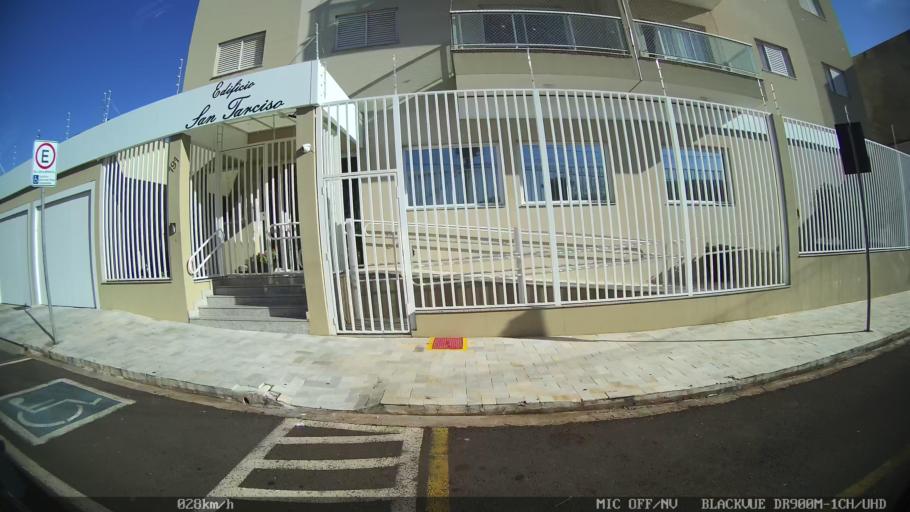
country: BR
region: Sao Paulo
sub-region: Franca
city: Franca
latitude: -20.5263
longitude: -47.4129
